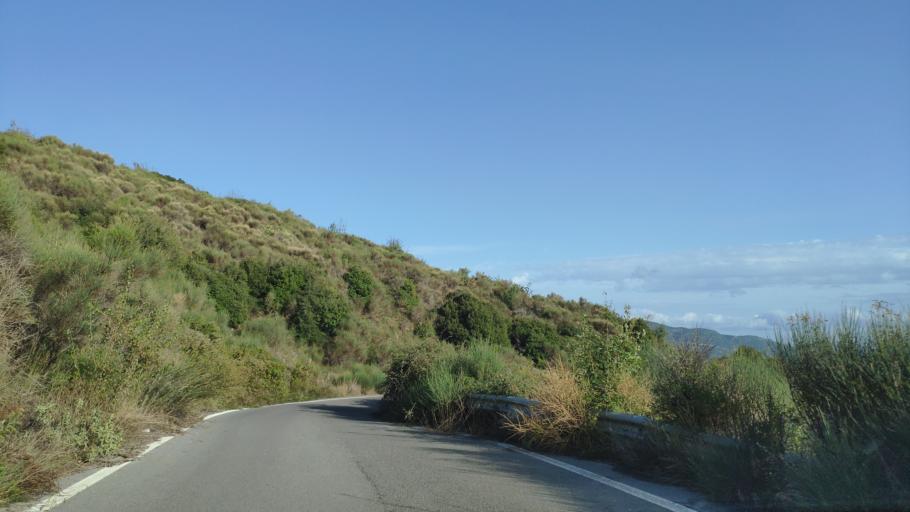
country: GR
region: Peloponnese
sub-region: Nomos Arkadias
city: Dimitsana
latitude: 37.5652
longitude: 22.0273
